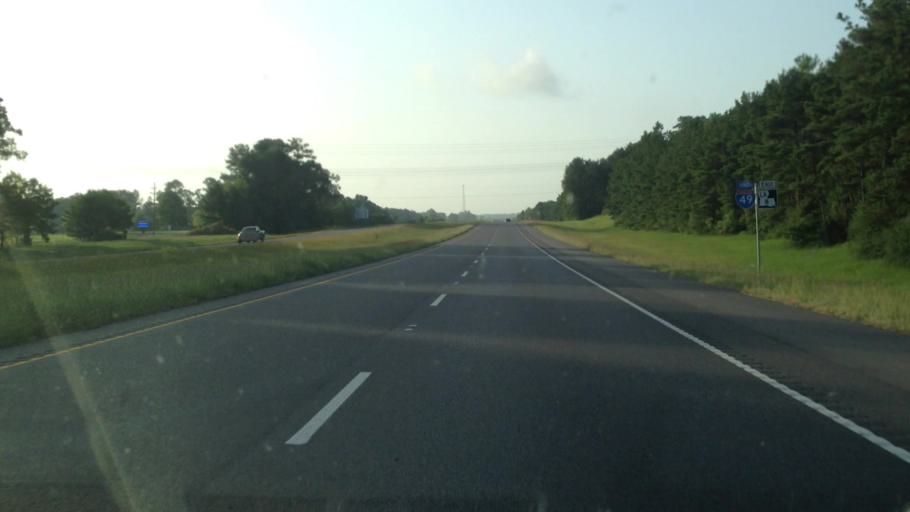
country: US
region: Louisiana
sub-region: Rapides Parish
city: Boyce
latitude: 31.4042
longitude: -92.7096
